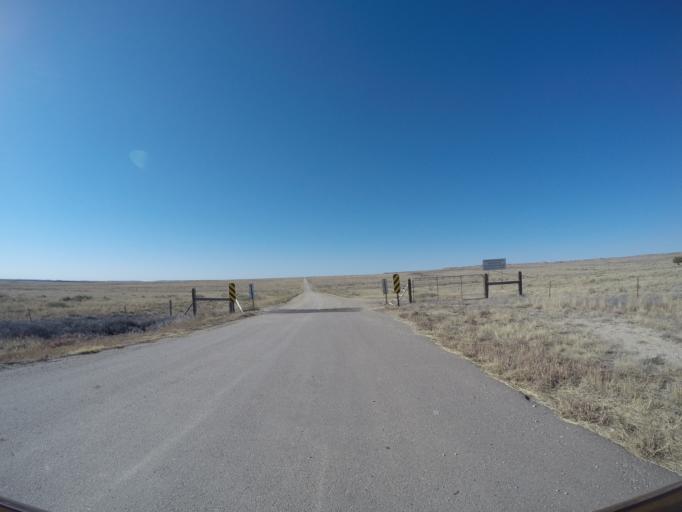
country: US
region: Colorado
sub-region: Otero County
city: La Junta
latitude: 37.8033
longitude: -103.4964
